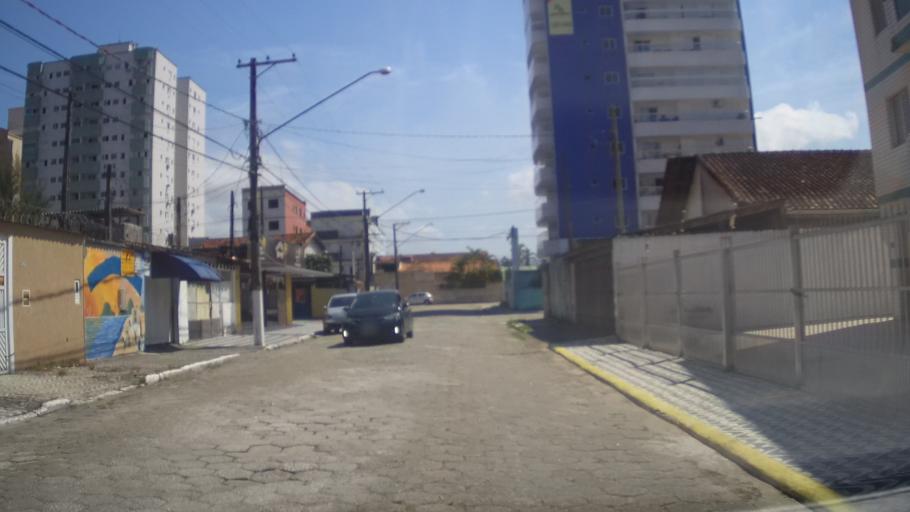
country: BR
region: Sao Paulo
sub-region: Praia Grande
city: Praia Grande
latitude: -24.0172
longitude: -46.4478
